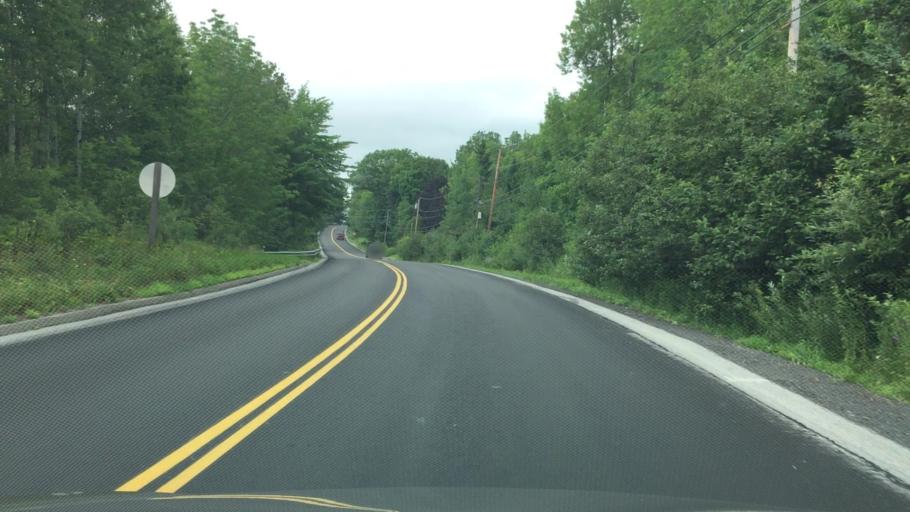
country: US
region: Maine
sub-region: Waldo County
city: Winterport
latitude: 44.6176
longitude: -68.8275
